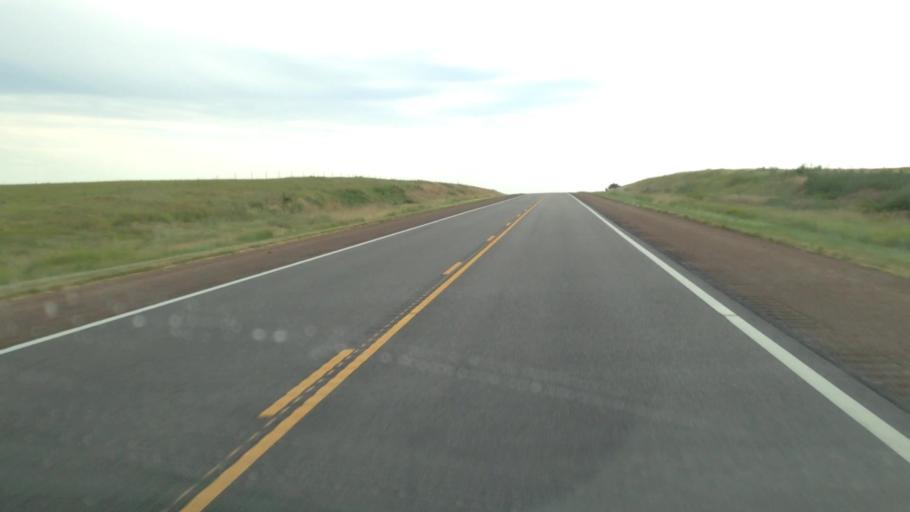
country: US
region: Kansas
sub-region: Coffey County
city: Burlington
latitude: 38.0501
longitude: -95.7391
